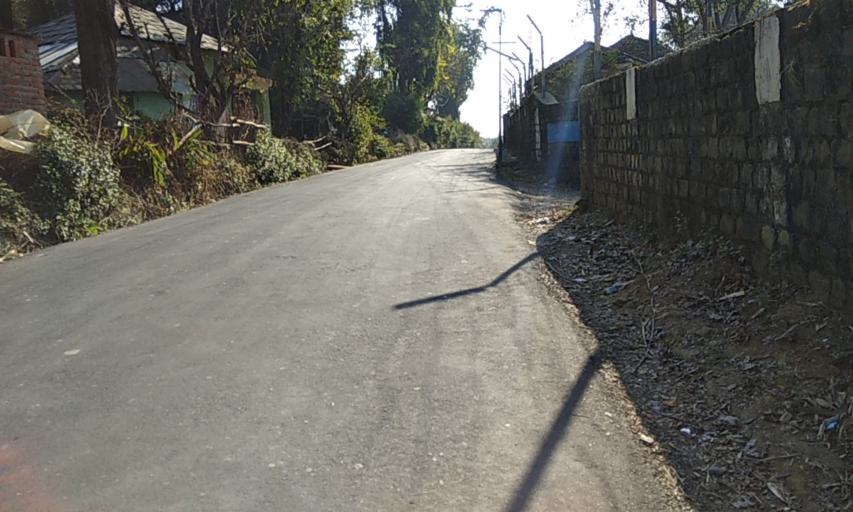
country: IN
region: Himachal Pradesh
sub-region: Kangra
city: Palampur
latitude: 32.1177
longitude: 76.5253
